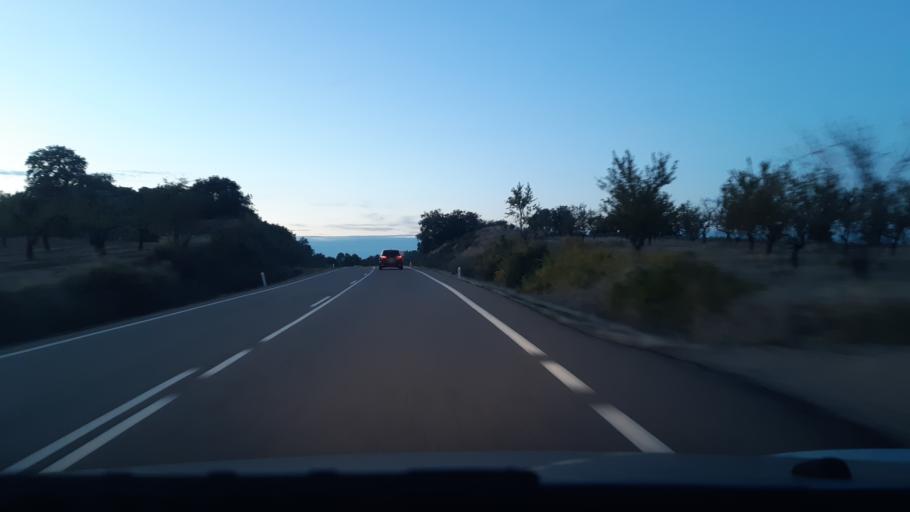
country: ES
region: Aragon
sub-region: Provincia de Teruel
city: Calaceite
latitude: 40.9723
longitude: 0.2061
